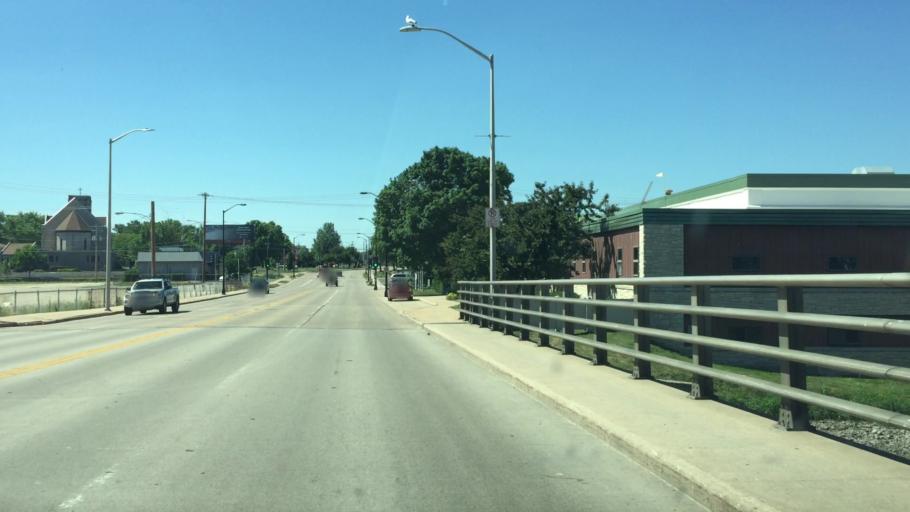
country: US
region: Wisconsin
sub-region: Winnebago County
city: Menasha
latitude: 44.1966
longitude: -88.4536
